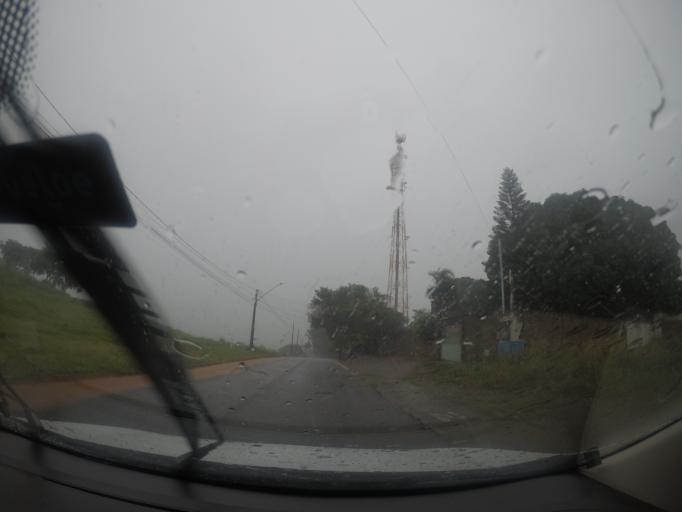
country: BR
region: Goias
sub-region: Goiania
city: Goiania
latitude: -16.6041
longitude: -49.3293
